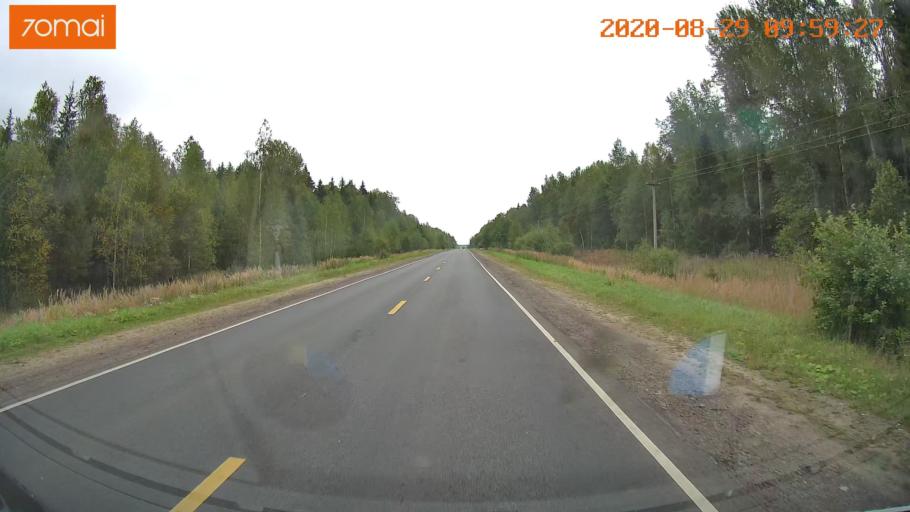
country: RU
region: Ivanovo
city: Zarechnyy
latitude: 57.4111
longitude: 42.3665
